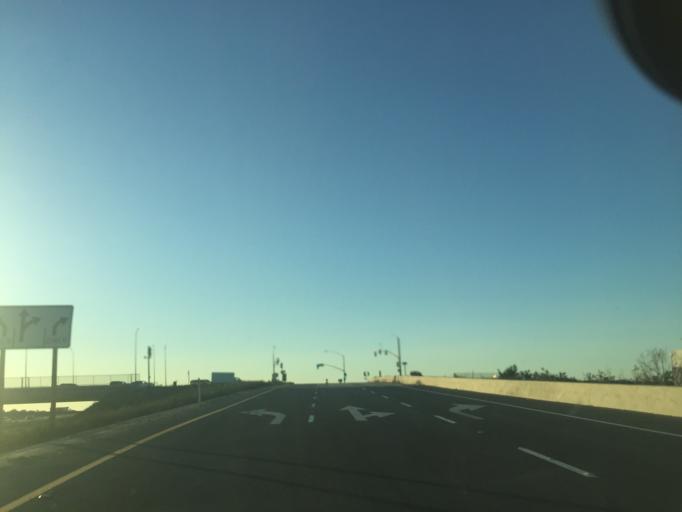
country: MX
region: Baja California
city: Tijuana
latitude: 32.5647
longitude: -116.9783
